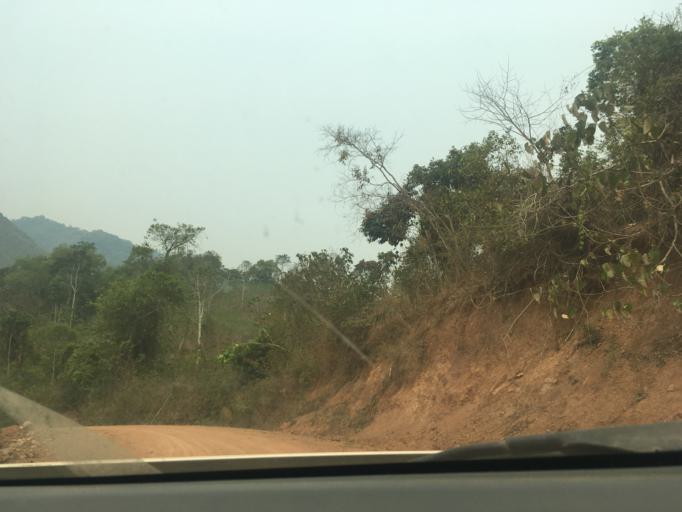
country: VN
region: Huyen Dien Bien
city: Thi Tran Muong Cha
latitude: 21.7415
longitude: 102.8380
